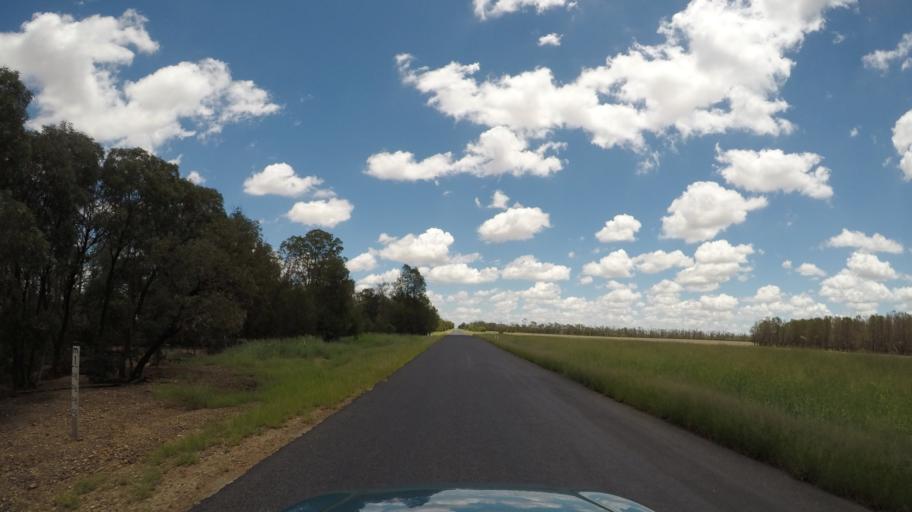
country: AU
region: Queensland
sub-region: Goondiwindi
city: Goondiwindi
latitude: -28.1700
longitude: 150.2107
